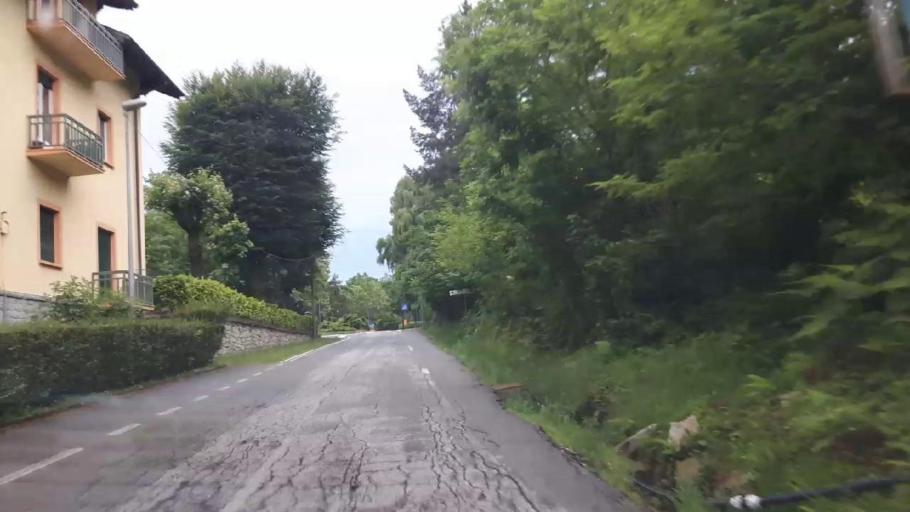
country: IT
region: Piedmont
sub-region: Provincia Verbano-Cusio-Ossola
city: Gignese
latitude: 45.8705
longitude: 8.5132
